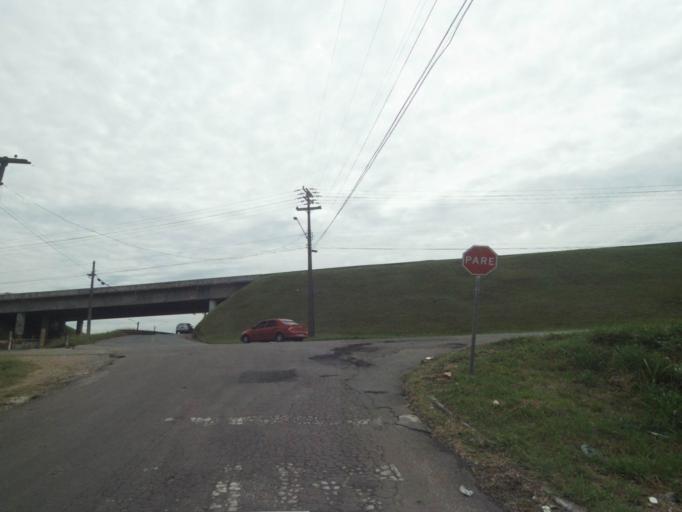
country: BR
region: Parana
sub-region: Pinhais
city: Pinhais
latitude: -25.4803
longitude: -49.1993
